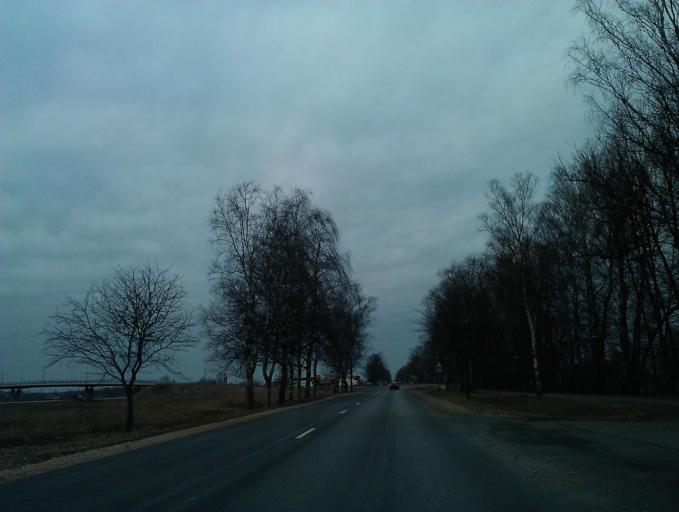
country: LV
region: Adazi
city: Adazi
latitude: 57.0664
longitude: 24.3228
